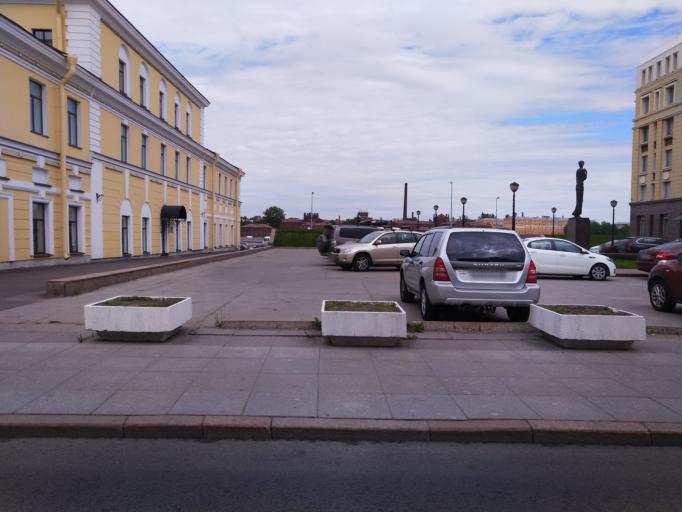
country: RU
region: St.-Petersburg
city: Centralniy
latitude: 59.9489
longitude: 30.3635
